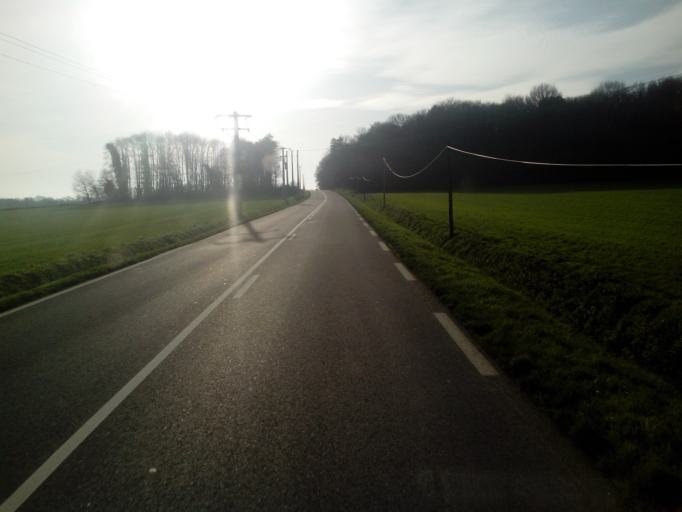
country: FR
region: Brittany
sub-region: Departement d'Ille-et-Vilaine
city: Gael
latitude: 48.1178
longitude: -2.2472
